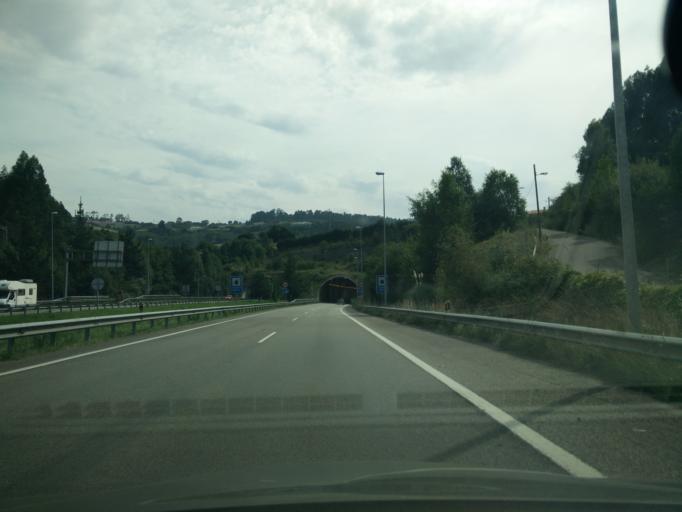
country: ES
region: Asturias
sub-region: Province of Asturias
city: Arriba
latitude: 43.5091
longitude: -5.5780
